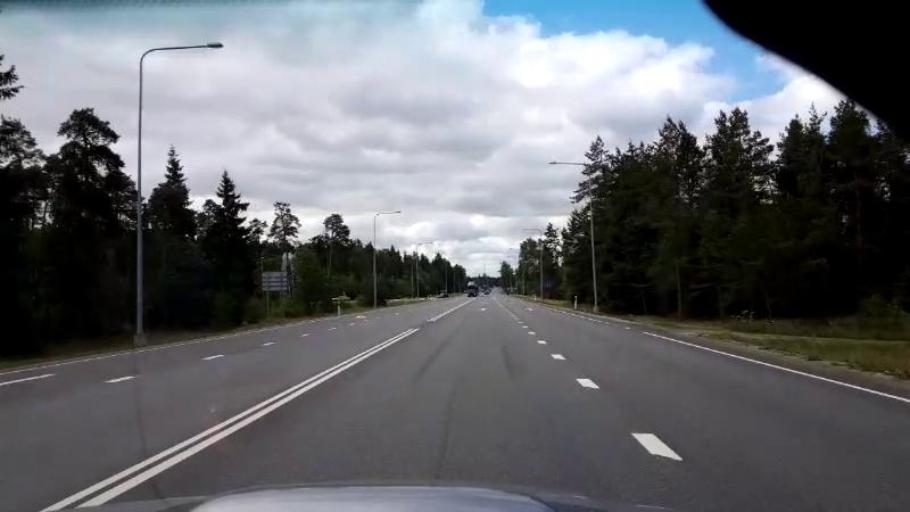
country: EE
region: Raplamaa
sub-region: Maerjamaa vald
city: Marjamaa
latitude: 58.9280
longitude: 24.4611
